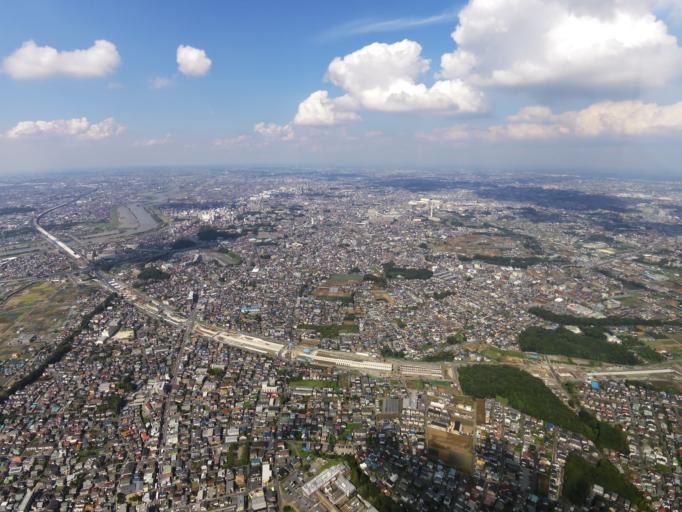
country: JP
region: Chiba
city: Matsudo
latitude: 35.7540
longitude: 139.9015
